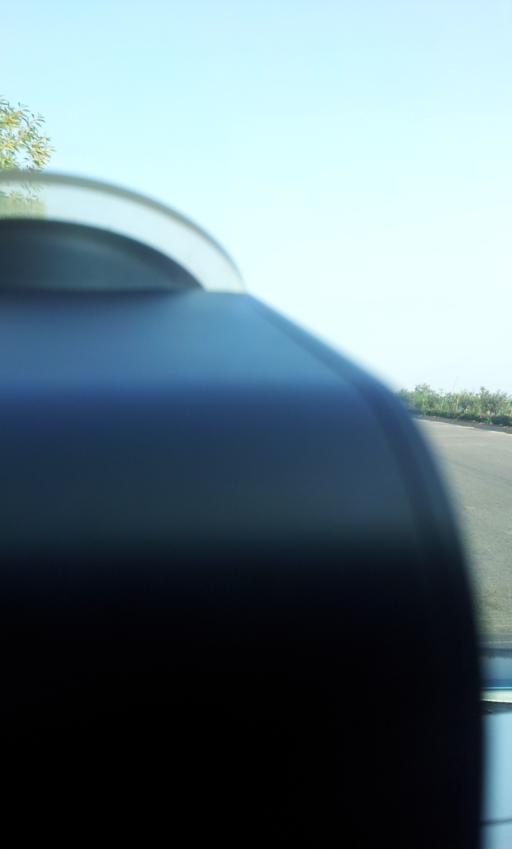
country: IN
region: Telangana
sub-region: Rangareddi
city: Secunderabad
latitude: 17.5748
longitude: 78.5702
